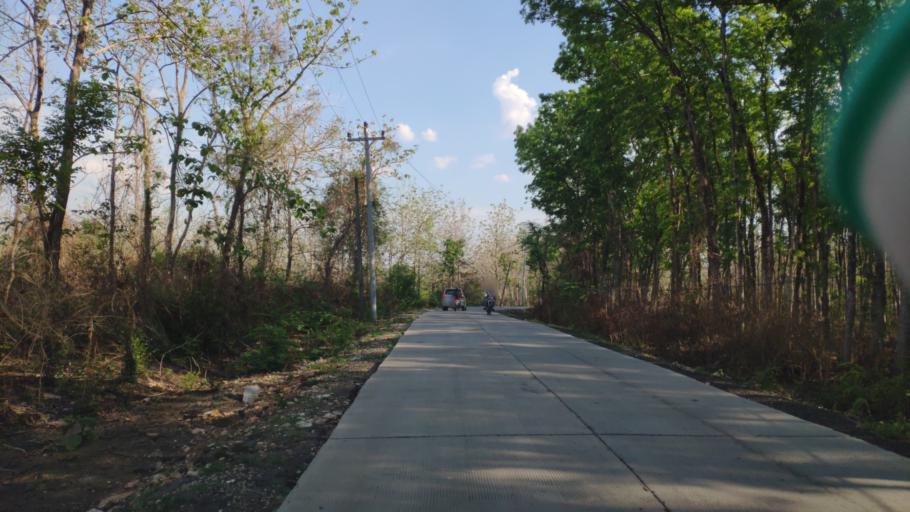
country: ID
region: Central Java
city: Ploso Wetan
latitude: -7.1714
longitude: 111.4092
